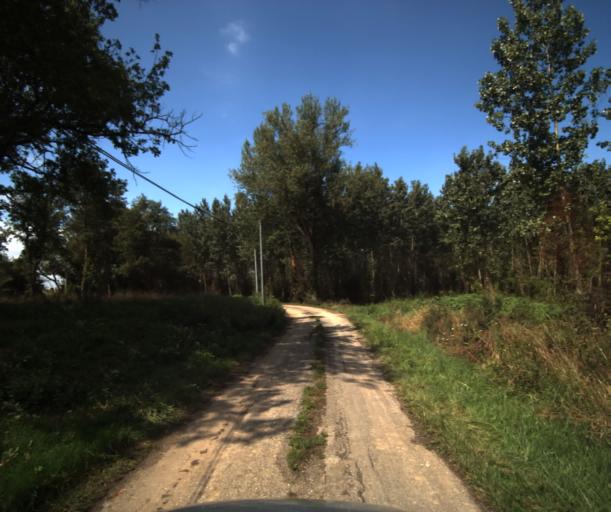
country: FR
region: Midi-Pyrenees
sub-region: Departement de la Haute-Garonne
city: Lacasse
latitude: 43.3889
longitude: 1.2489
